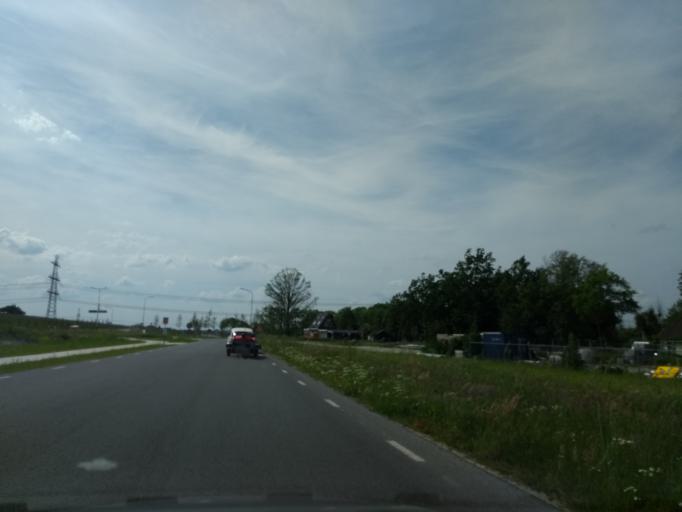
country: NL
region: Groningen
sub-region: Gemeente Zuidhorn
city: Aduard
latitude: 53.2459
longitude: 6.4789
